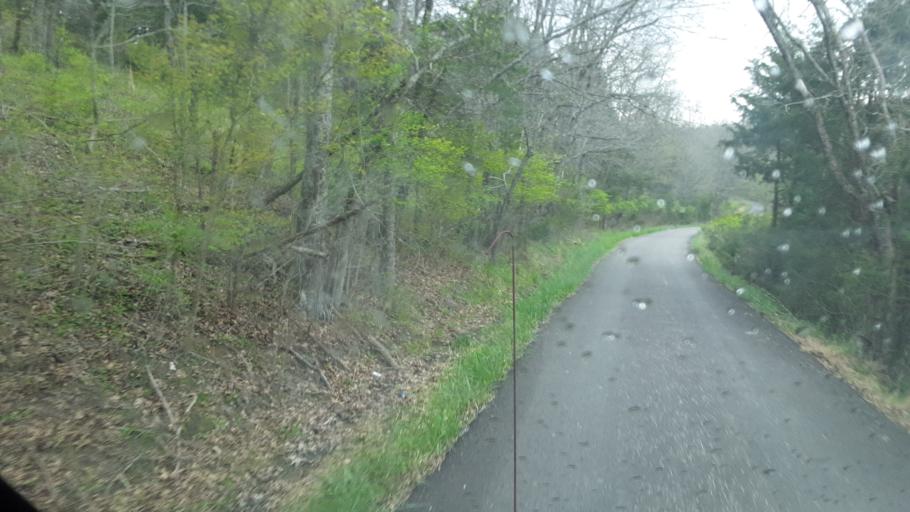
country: US
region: Kentucky
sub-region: Owen County
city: Owenton
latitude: 38.6729
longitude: -84.7968
